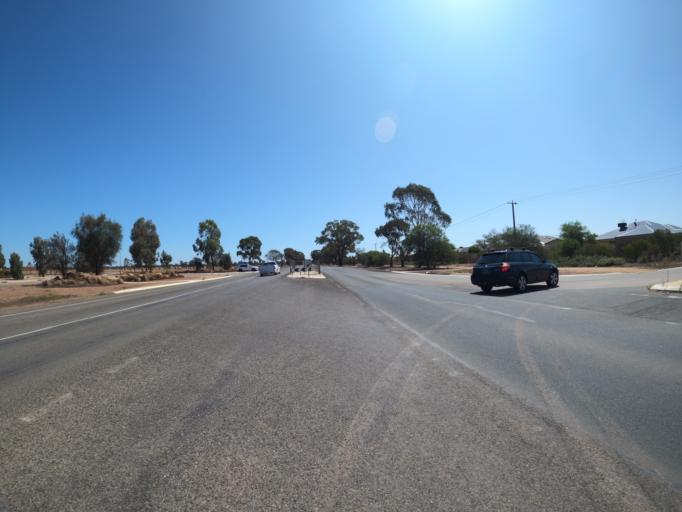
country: AU
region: Victoria
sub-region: Moira
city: Yarrawonga
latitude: -36.0113
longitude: 146.0255
